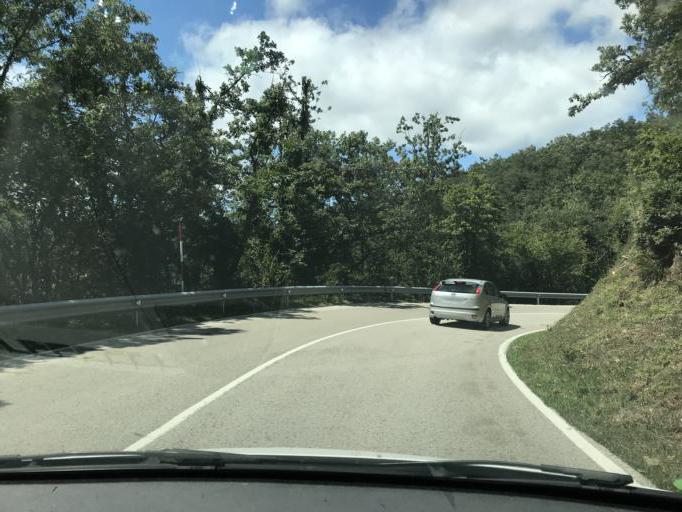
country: ES
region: Cantabria
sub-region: Provincia de Cantabria
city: Cabezon de Liebana
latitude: 43.0756
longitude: -4.4821
